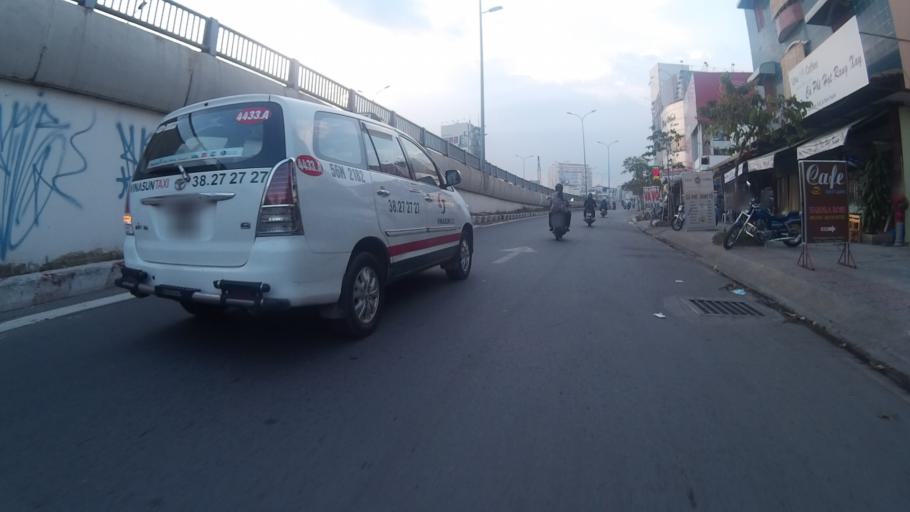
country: VN
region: Ho Chi Minh City
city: Quan Mot
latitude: 10.7894
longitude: 106.7151
